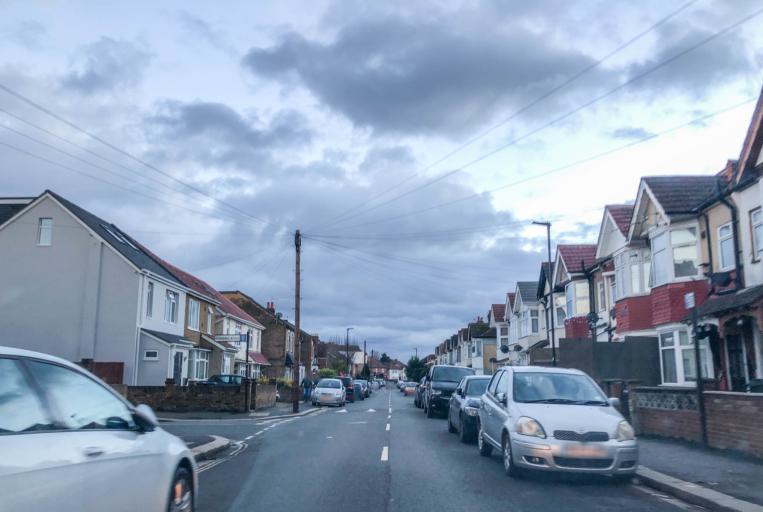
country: GB
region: England
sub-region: Greater London
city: Hounslow
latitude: 51.4615
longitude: -0.3714
